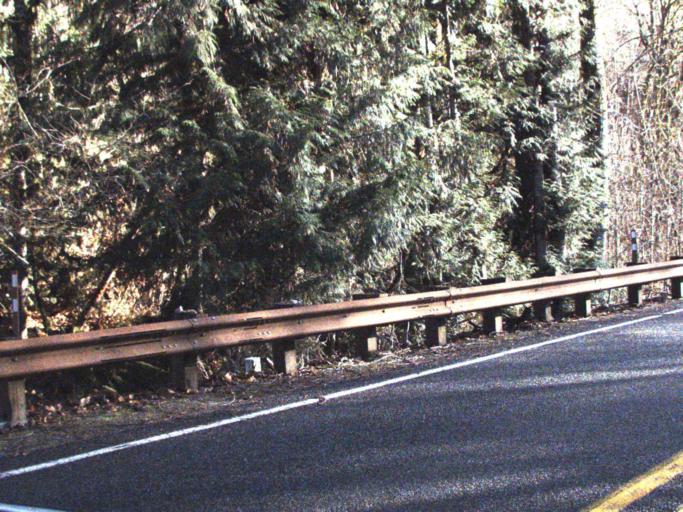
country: US
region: Washington
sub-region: Snohomish County
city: Darrington
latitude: 48.4468
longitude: -121.5838
